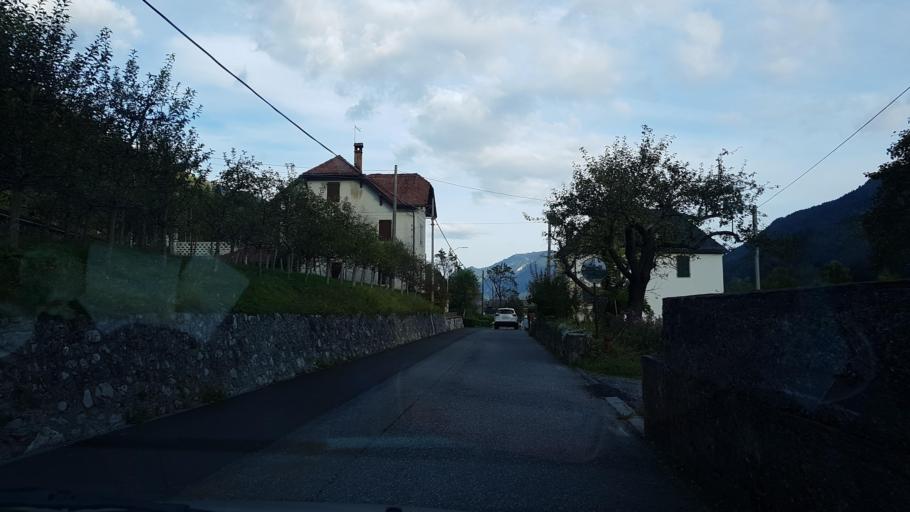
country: IT
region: Friuli Venezia Giulia
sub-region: Provincia di Udine
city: Pieria-Prato Carnico
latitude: 46.5215
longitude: 12.7781
